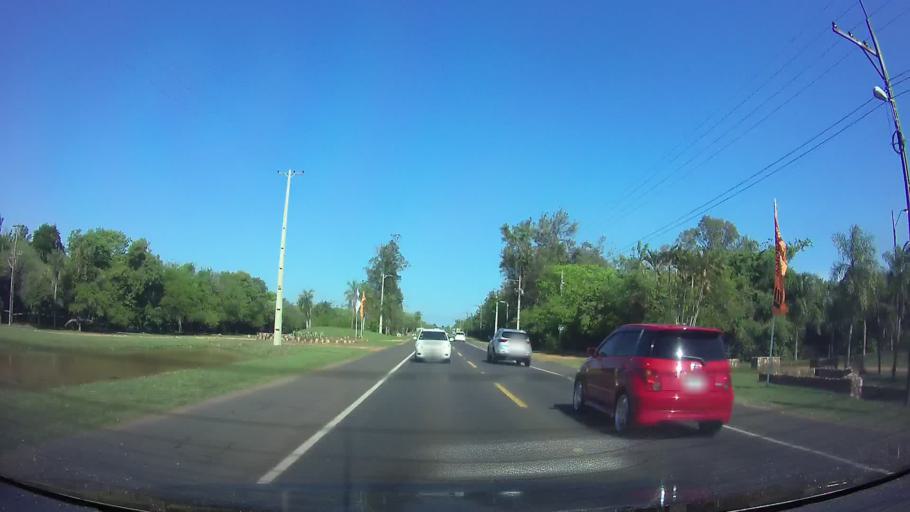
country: PY
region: Central
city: Itaugua
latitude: -25.3655
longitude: -57.3139
